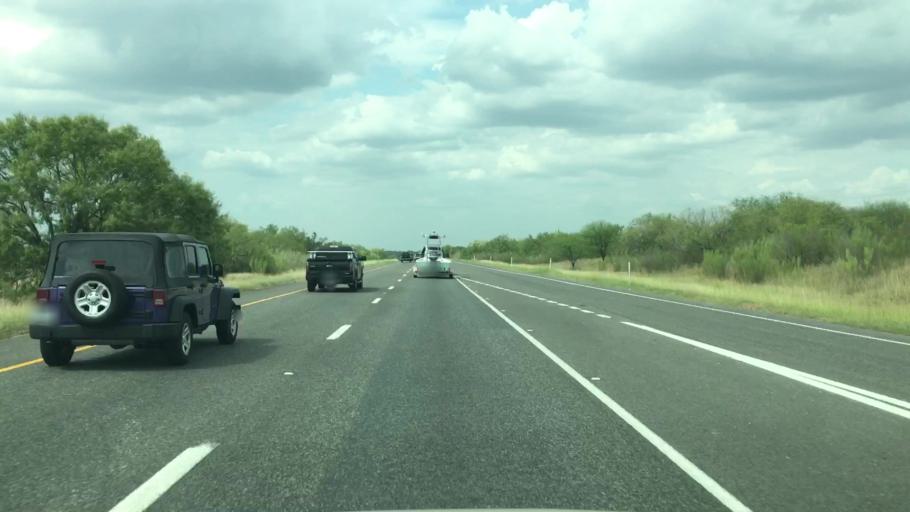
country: US
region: Texas
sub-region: Atascosa County
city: Pleasanton
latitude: 28.9193
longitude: -98.4347
